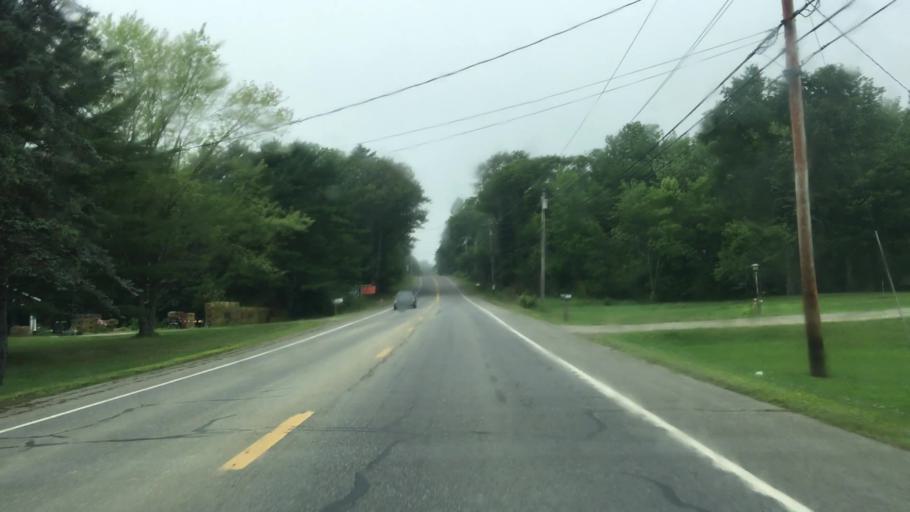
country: US
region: Maine
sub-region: Lincoln County
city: Wiscasset
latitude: 44.0558
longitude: -69.6844
